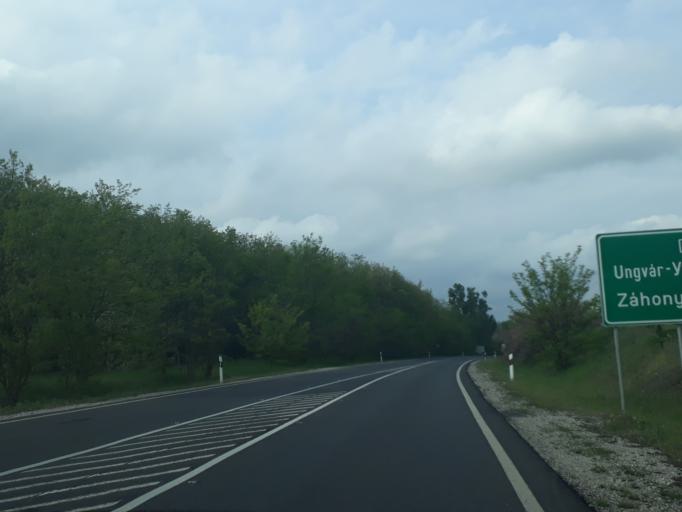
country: HU
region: Szabolcs-Szatmar-Bereg
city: Nyirtass
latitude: 48.1106
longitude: 21.9895
